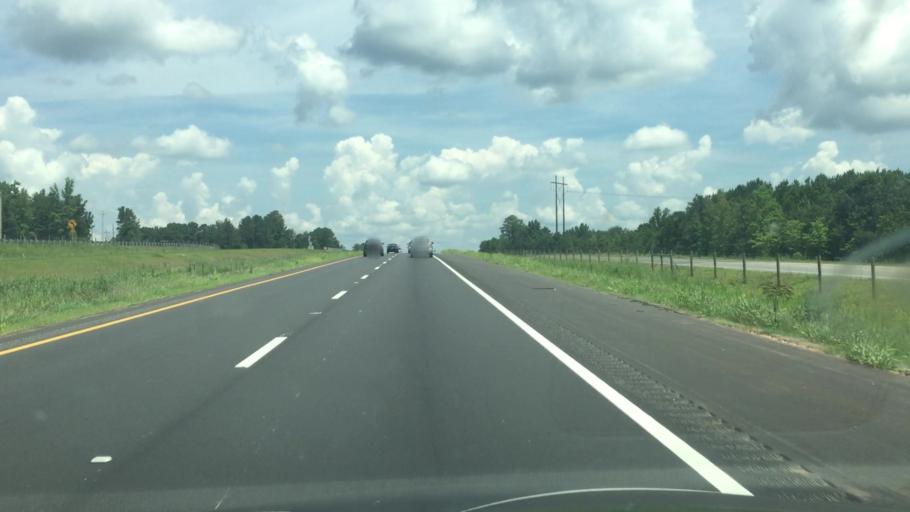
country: US
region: North Carolina
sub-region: Richmond County
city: Ellerbe
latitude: 35.0332
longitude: -79.7691
